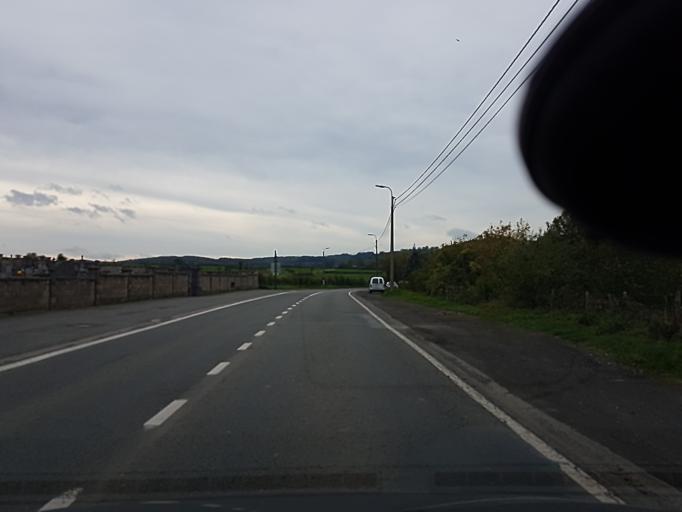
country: BE
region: Wallonia
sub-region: Province de Liege
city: Theux
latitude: 50.5362
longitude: 5.8039
